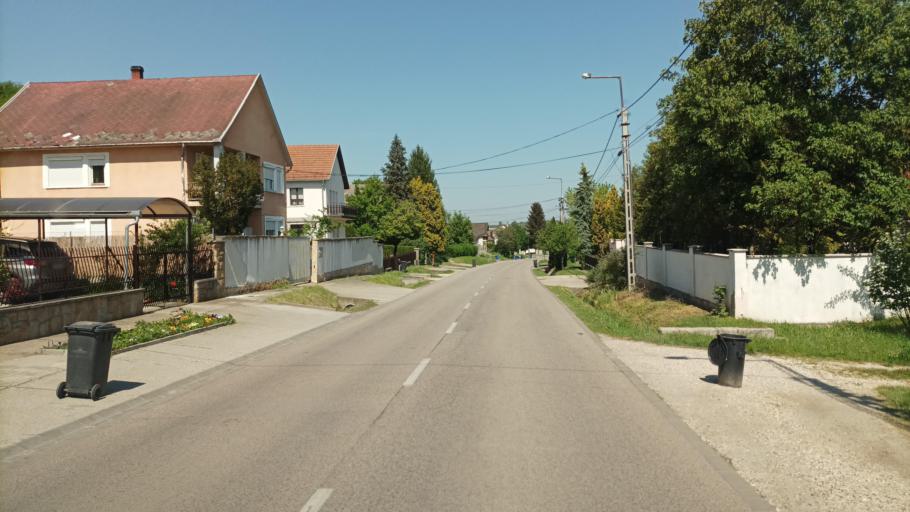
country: HU
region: Pest
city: Suelysap
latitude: 47.4443
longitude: 19.5273
